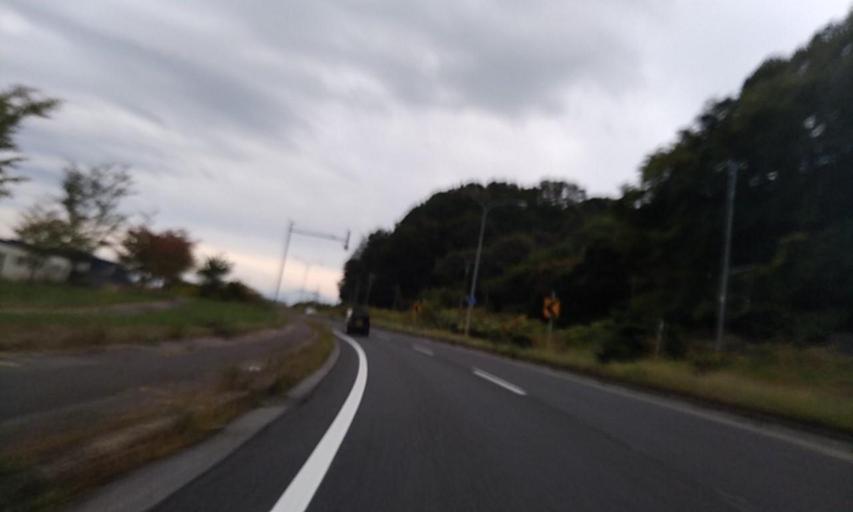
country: JP
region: Hokkaido
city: Abashiri
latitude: 44.0094
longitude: 144.2810
